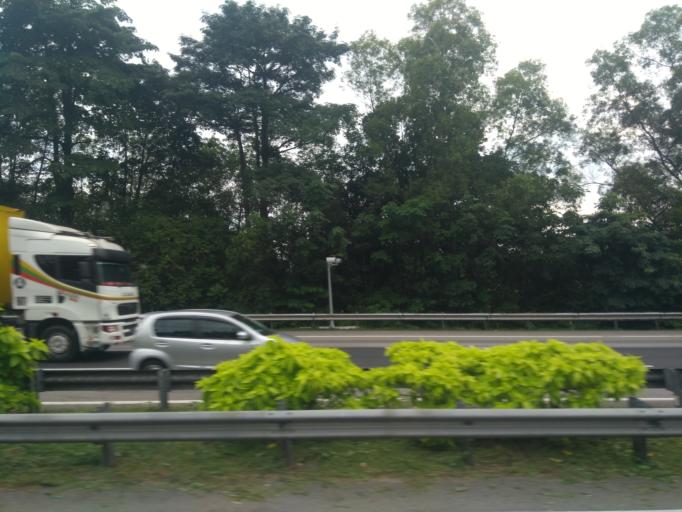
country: MY
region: Melaka
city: Pulau Sebang
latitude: 2.4335
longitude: 102.2050
